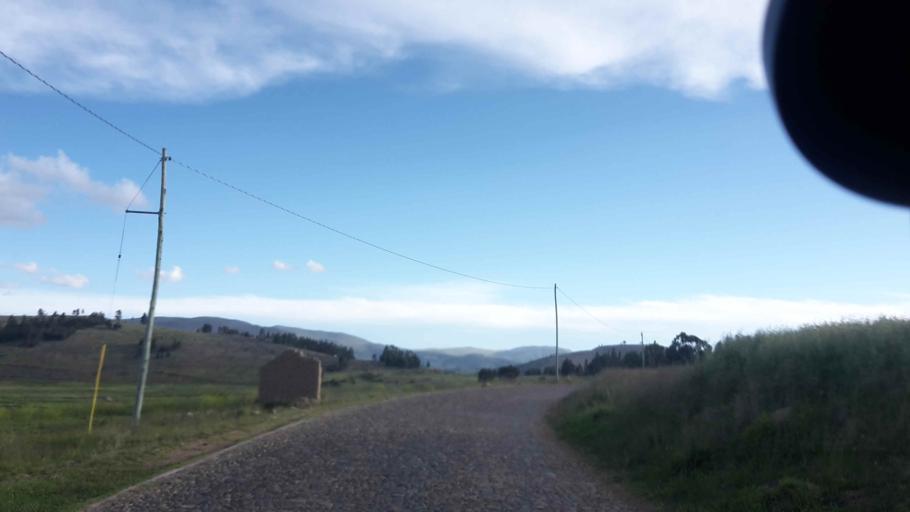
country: BO
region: Cochabamba
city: Arani
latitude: -17.5350
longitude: -65.6605
